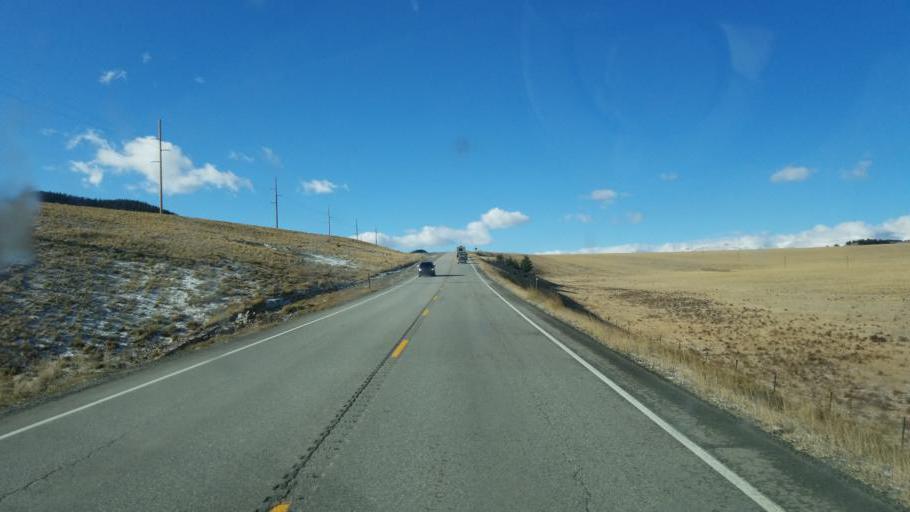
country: US
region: Colorado
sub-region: Park County
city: Fairplay
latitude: 39.2889
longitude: -105.9094
